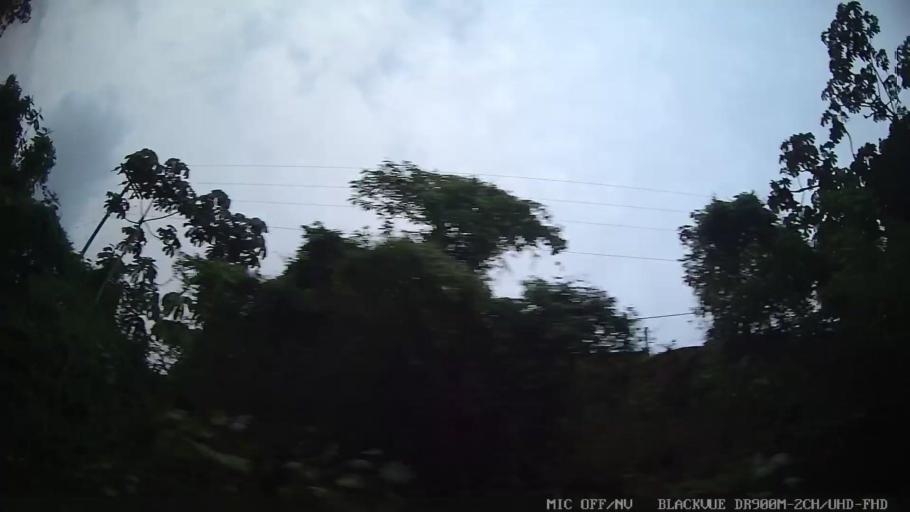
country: BR
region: Sao Paulo
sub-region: Braganca Paulista
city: Braganca Paulista
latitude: -22.9491
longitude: -46.5854
